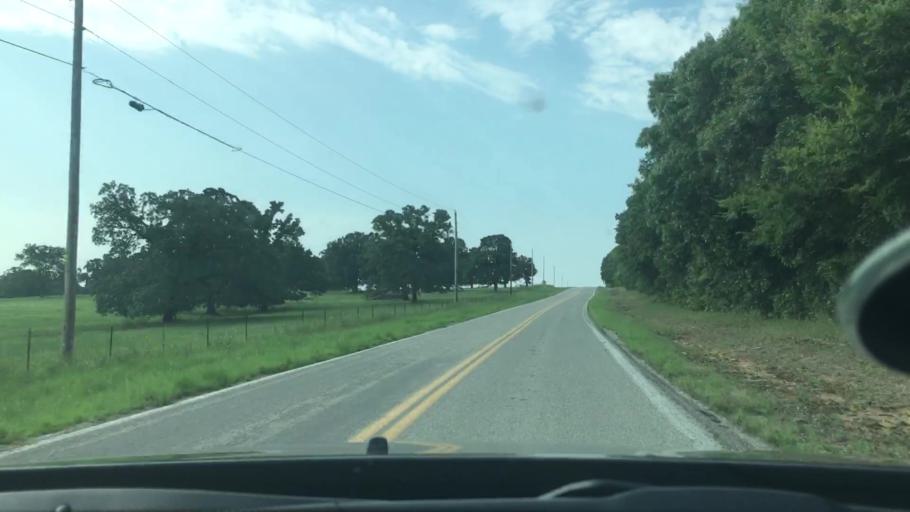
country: US
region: Oklahoma
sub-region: Johnston County
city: Tishomingo
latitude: 34.1973
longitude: -96.5773
